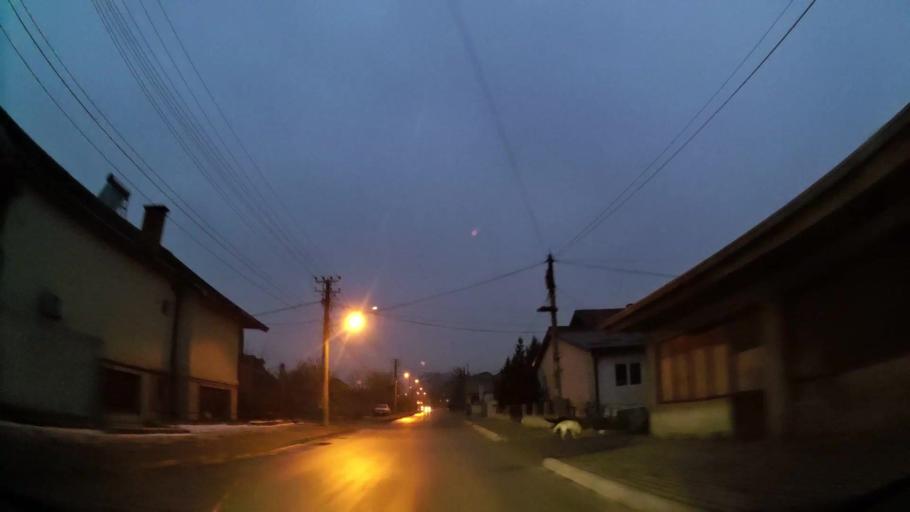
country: MK
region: Kisela Voda
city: Kisela Voda
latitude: 41.9681
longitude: 21.4887
